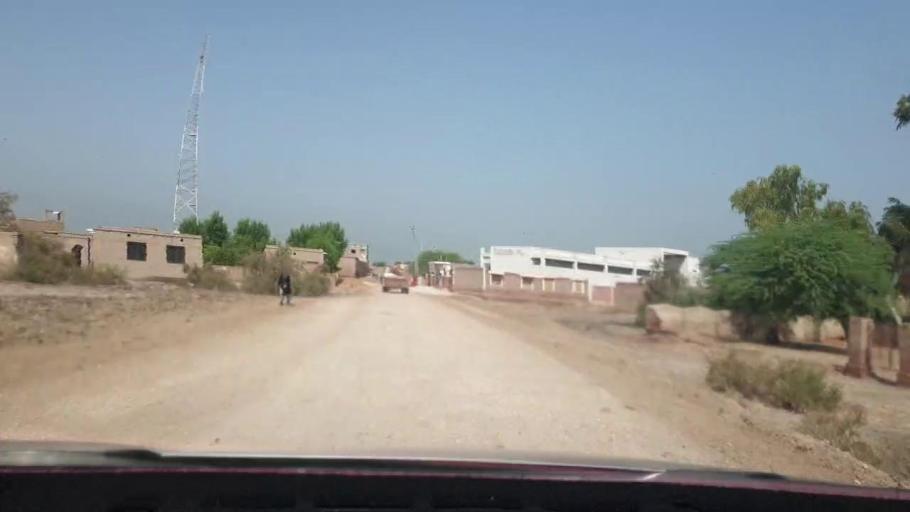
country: PK
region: Sindh
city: Nasirabad
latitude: 27.4248
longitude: 67.9277
